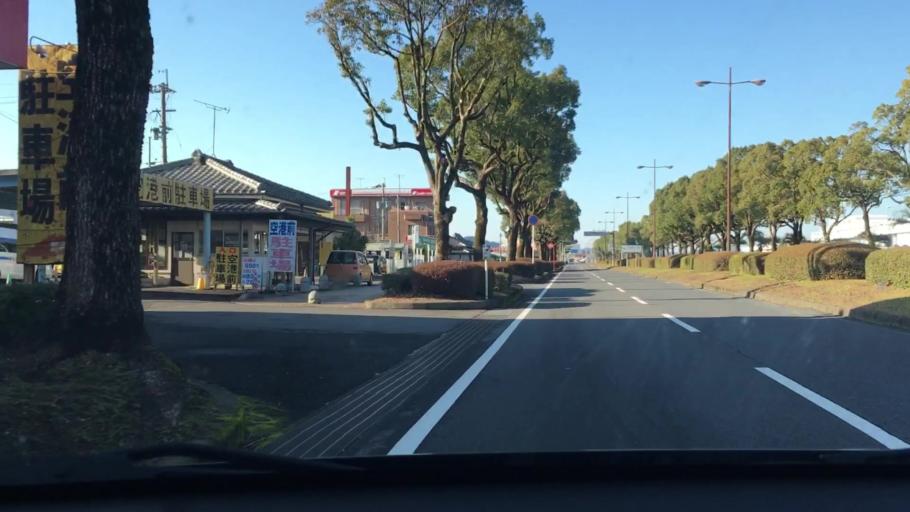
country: JP
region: Kagoshima
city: Kokubu-matsuki
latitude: 31.7972
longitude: 130.7169
